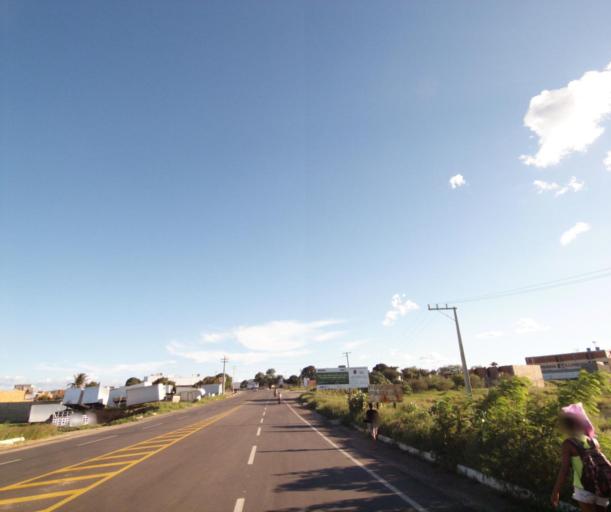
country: BR
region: Bahia
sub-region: Guanambi
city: Guanambi
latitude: -14.2104
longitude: -42.7646
